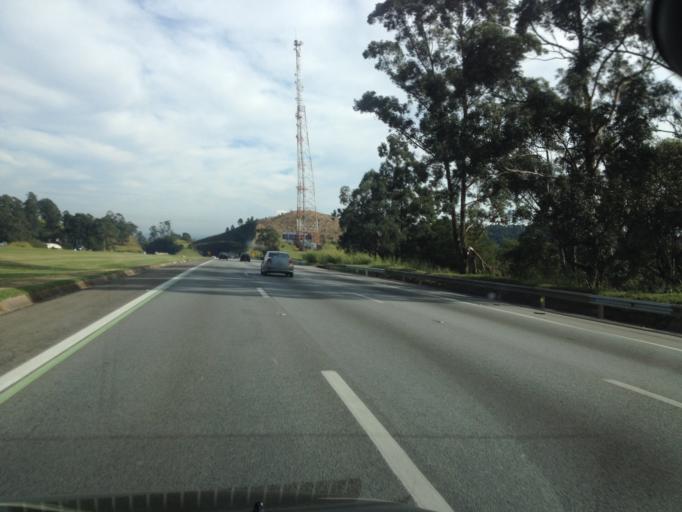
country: BR
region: Sao Paulo
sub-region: Mairinque
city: Mairinque
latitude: -23.4180
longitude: -47.2533
